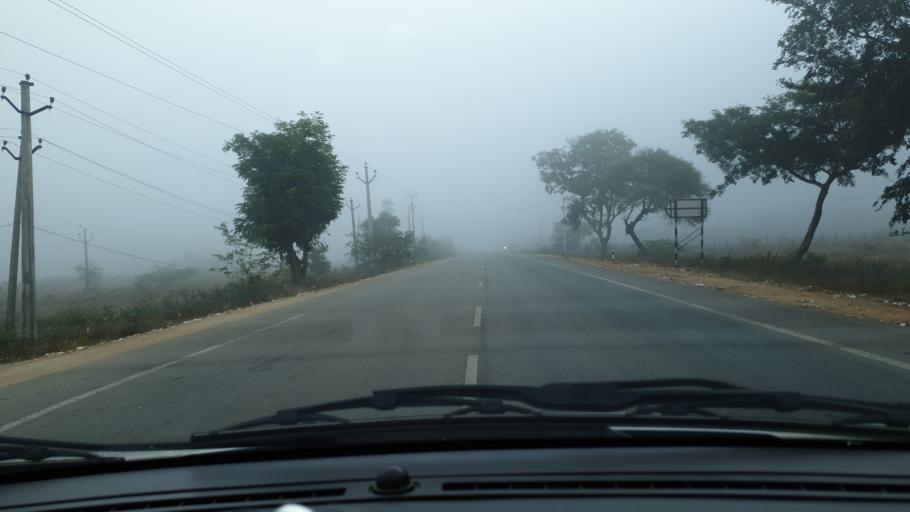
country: IN
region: Telangana
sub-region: Mahbubnagar
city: Nagar Karnul
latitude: 16.6647
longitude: 78.5583
